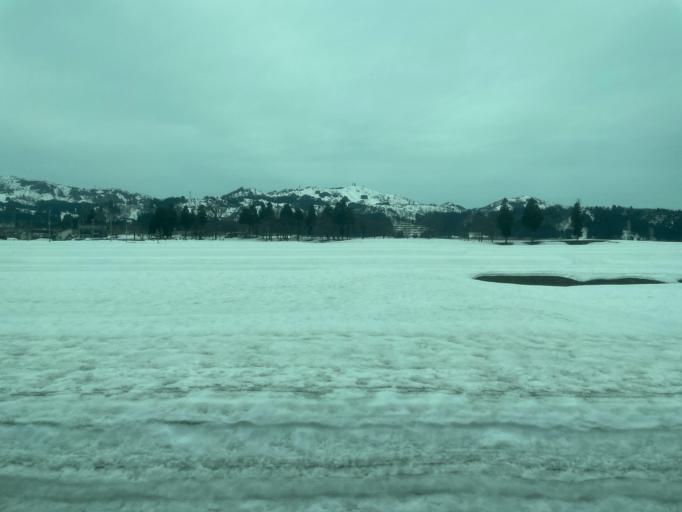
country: JP
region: Niigata
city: Shiozawa
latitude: 37.0493
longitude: 138.8614
